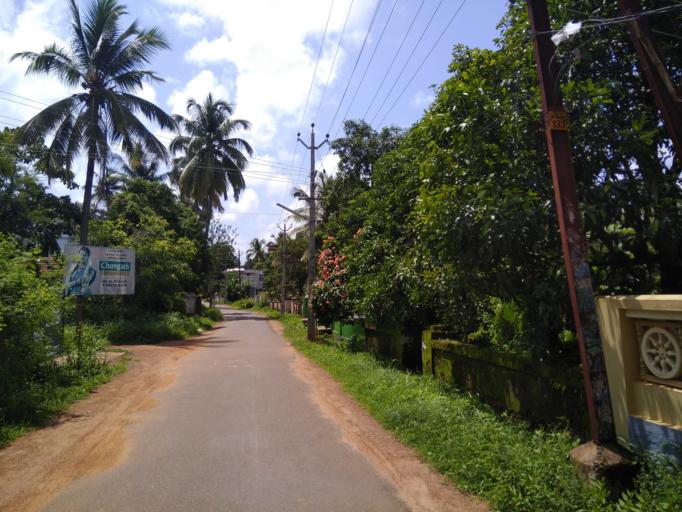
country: IN
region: Kerala
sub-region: Thrissur District
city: Avanoor
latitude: 10.5481
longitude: 76.1536
